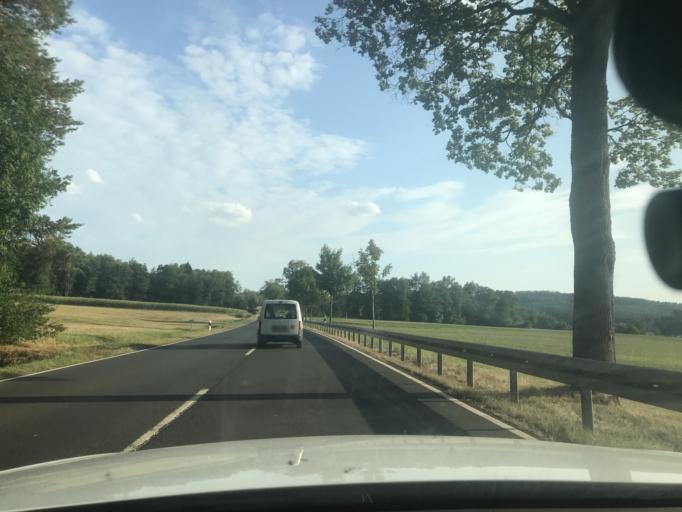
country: DE
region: Bavaria
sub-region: Upper Franconia
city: Pegnitz
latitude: 49.7887
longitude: 11.5786
